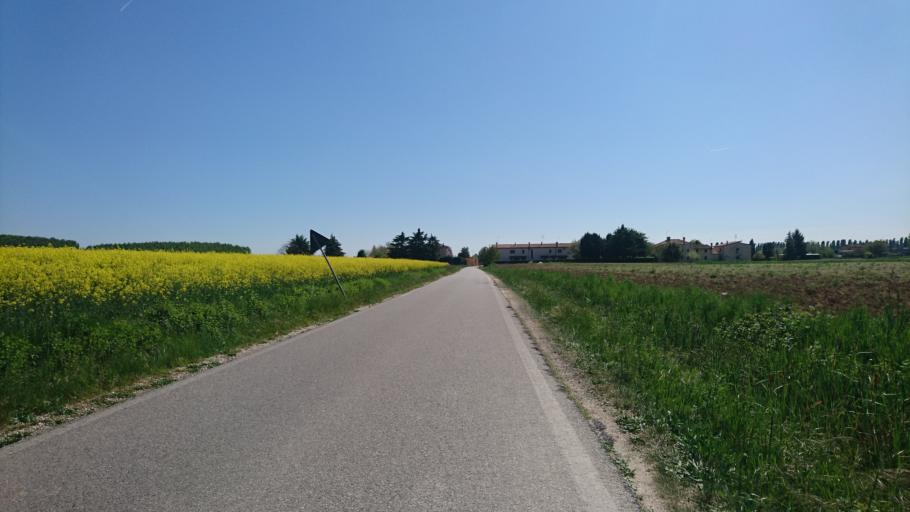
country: IT
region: Veneto
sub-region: Provincia di Treviso
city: Conscio
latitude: 45.5951
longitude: 12.2777
